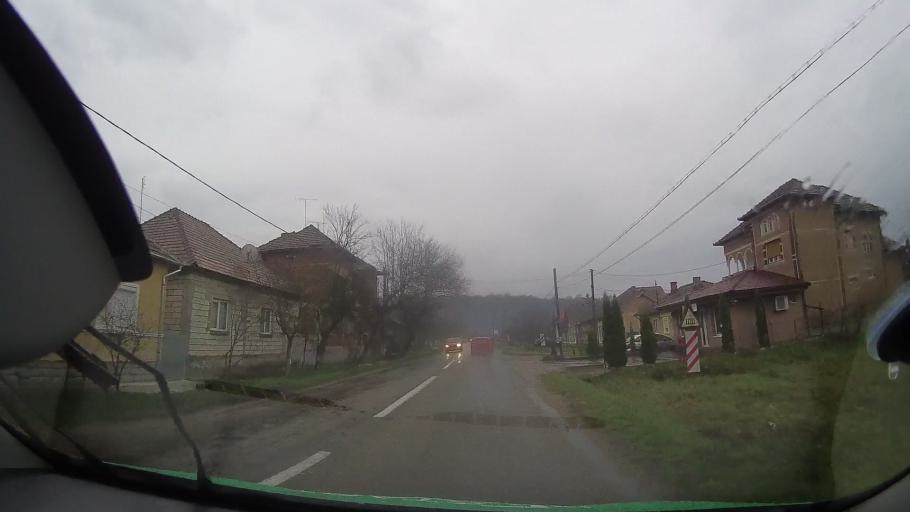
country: RO
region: Bihor
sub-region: Comuna Holod
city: Holod
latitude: 46.7841
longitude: 22.1317
